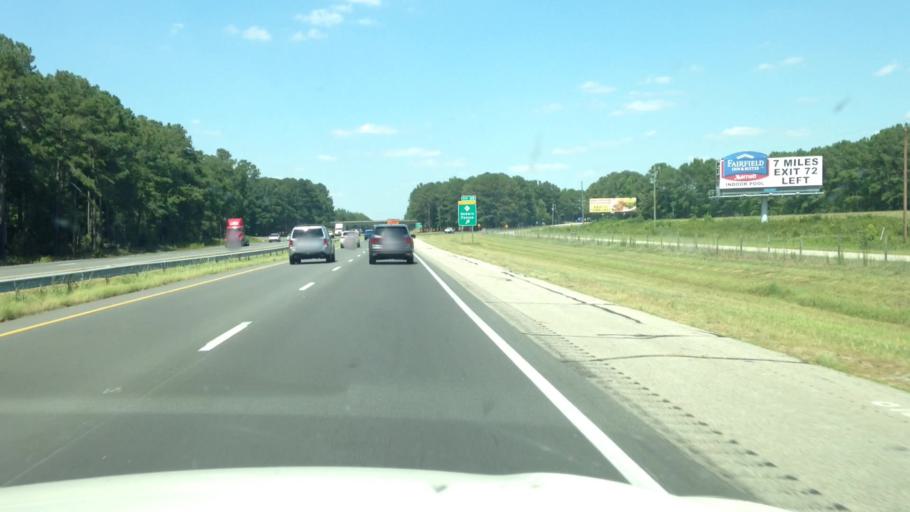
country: US
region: North Carolina
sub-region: Harnett County
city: Dunn
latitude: 35.2000
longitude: -78.6726
